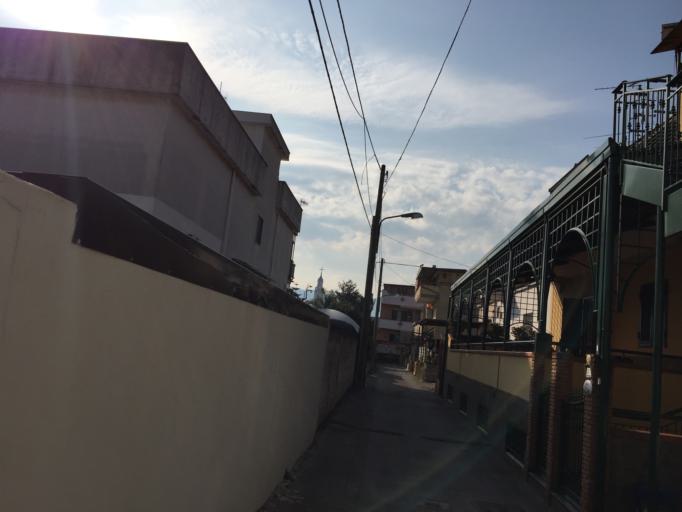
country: IT
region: Campania
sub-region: Provincia di Napoli
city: Pompei
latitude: 40.7547
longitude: 14.4973
